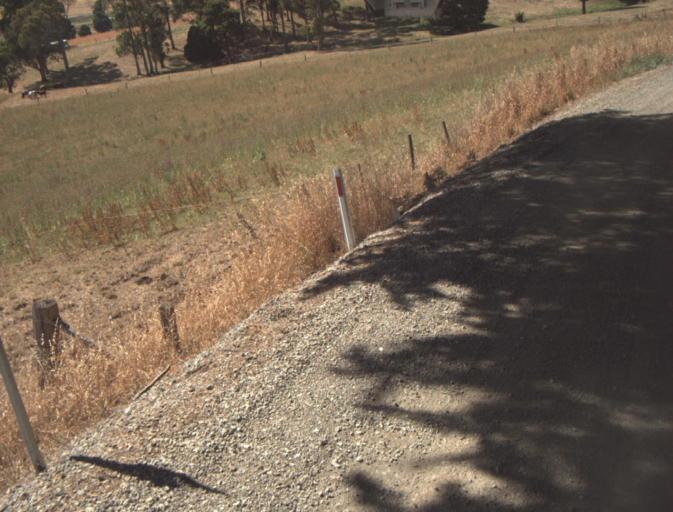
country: AU
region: Tasmania
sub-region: Launceston
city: Mayfield
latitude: -41.2321
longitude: 147.2522
